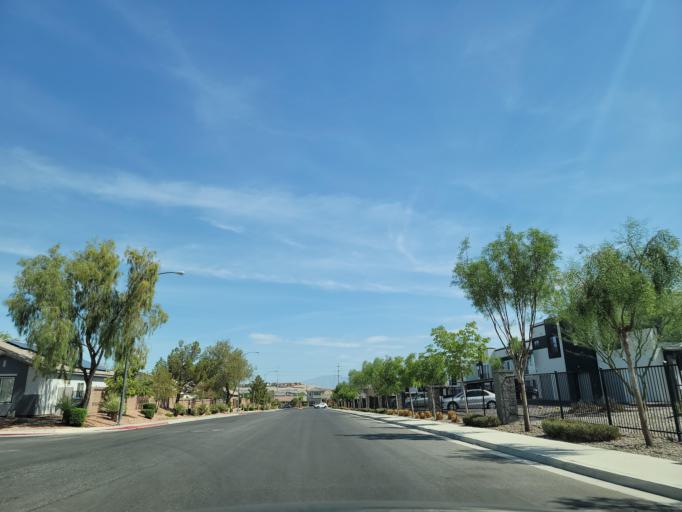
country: US
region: Nevada
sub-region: Clark County
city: Spring Valley
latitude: 36.0798
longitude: -115.2839
